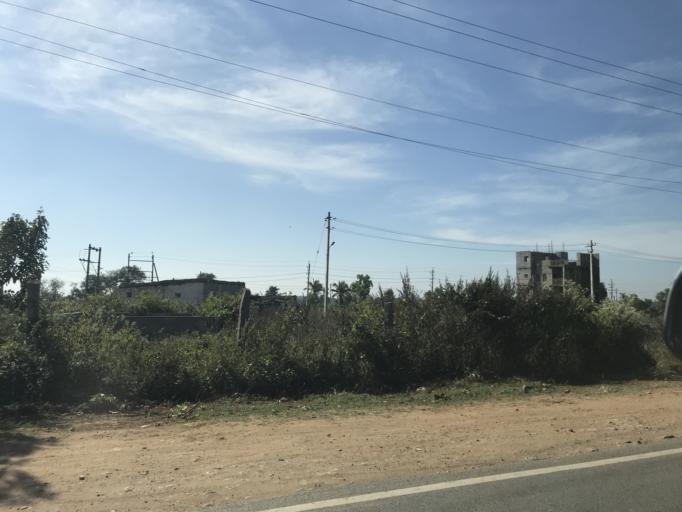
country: IN
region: Karnataka
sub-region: Mysore
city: Mysore
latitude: 12.2001
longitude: 76.5515
